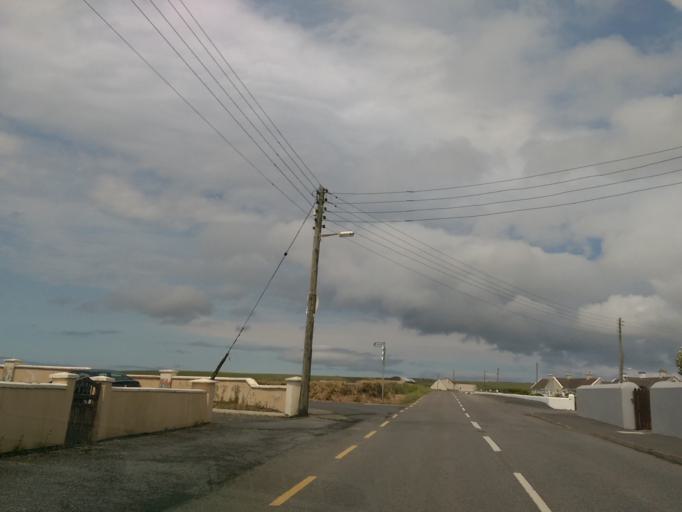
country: IE
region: Munster
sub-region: An Clar
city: Kilrush
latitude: 52.6861
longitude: -9.6415
